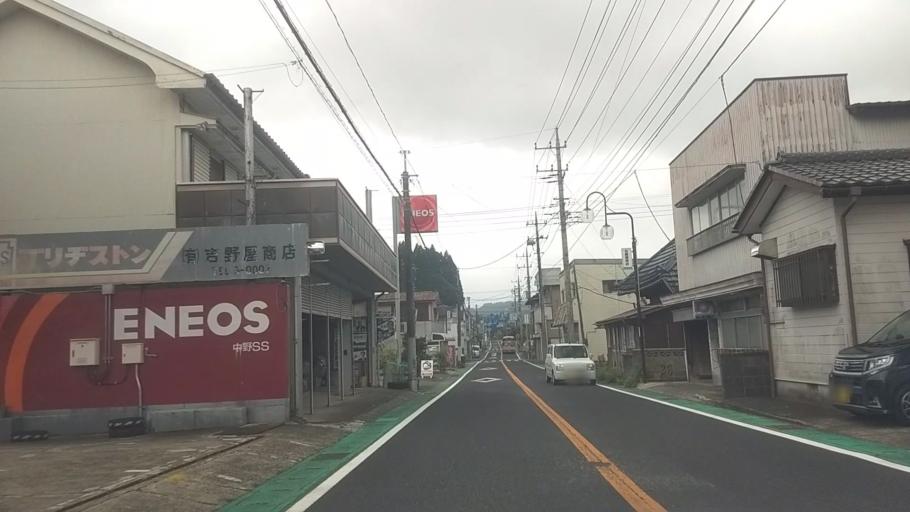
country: JP
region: Chiba
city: Katsuura
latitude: 35.2512
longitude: 140.1994
